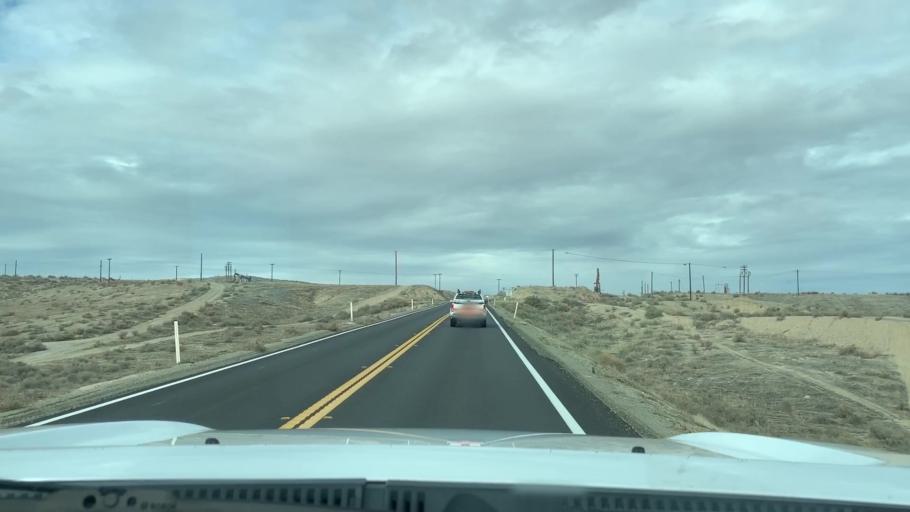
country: US
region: California
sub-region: Kern County
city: South Taft
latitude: 35.1124
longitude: -119.4269
